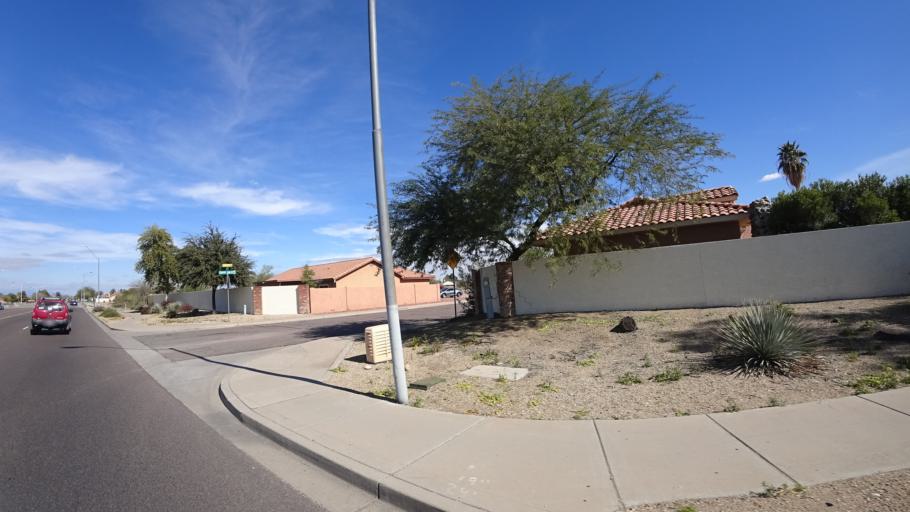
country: US
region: Arizona
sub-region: Maricopa County
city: Peoria
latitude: 33.6197
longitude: -112.2024
